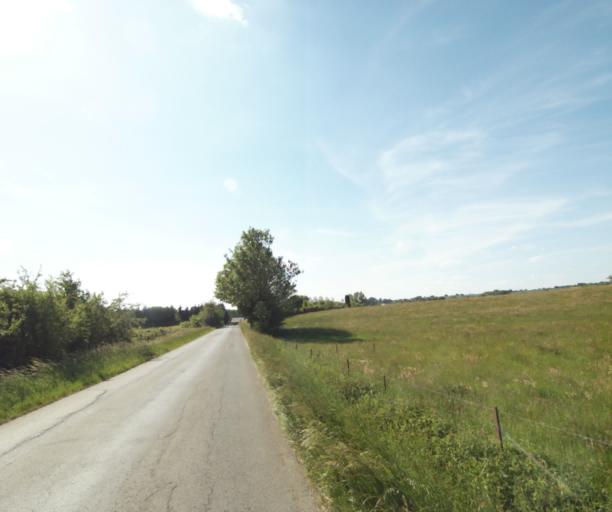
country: FR
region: Champagne-Ardenne
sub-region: Departement des Ardennes
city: Warcq
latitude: 49.7921
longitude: 4.6865
